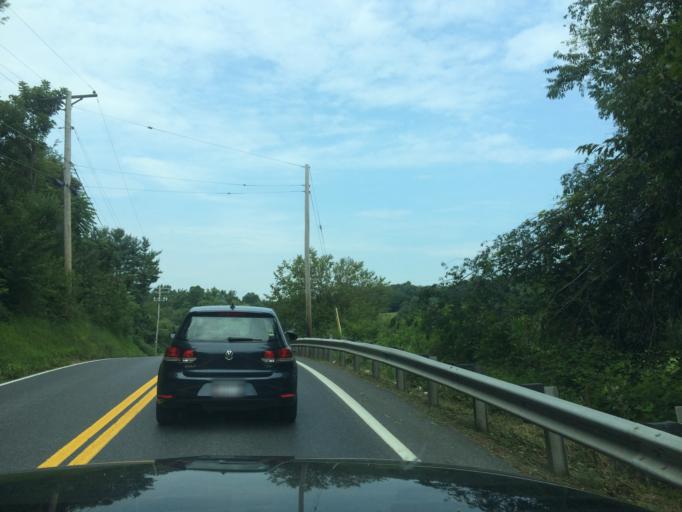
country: US
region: Maryland
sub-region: Carroll County
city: Sykesville
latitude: 39.4125
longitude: -77.0119
